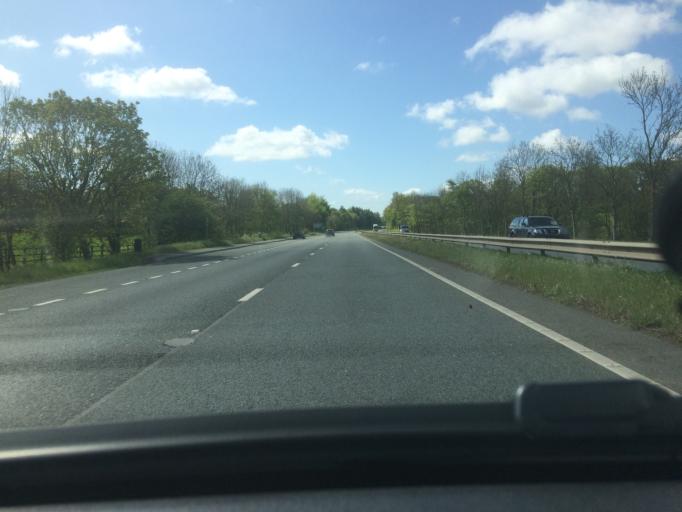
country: GB
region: Wales
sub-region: Wrexham
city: Coedpoeth
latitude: 53.0387
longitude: -3.0309
